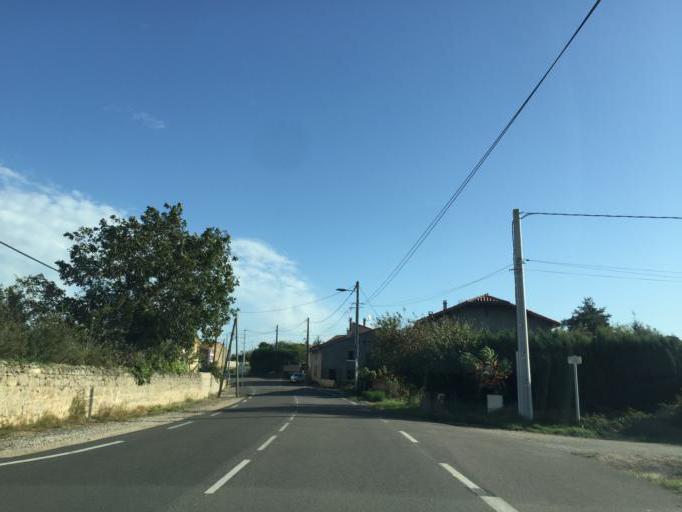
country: FR
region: Rhone-Alpes
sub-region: Departement de la Loire
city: Perigneux
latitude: 45.4610
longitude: 4.1156
